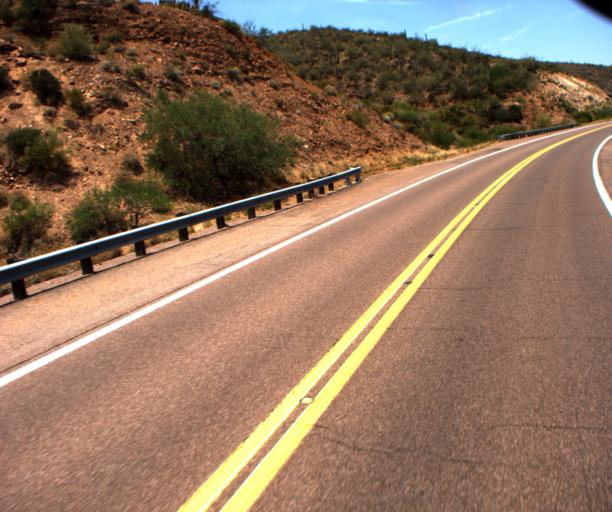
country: US
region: Arizona
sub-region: Gila County
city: Tonto Basin
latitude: 33.6847
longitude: -111.1720
